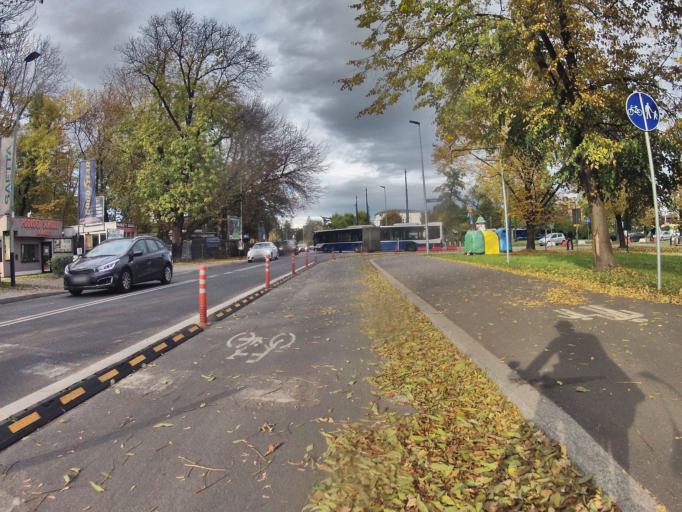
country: PL
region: Lesser Poland Voivodeship
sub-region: Krakow
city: Krakow
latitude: 50.0623
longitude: 19.9023
